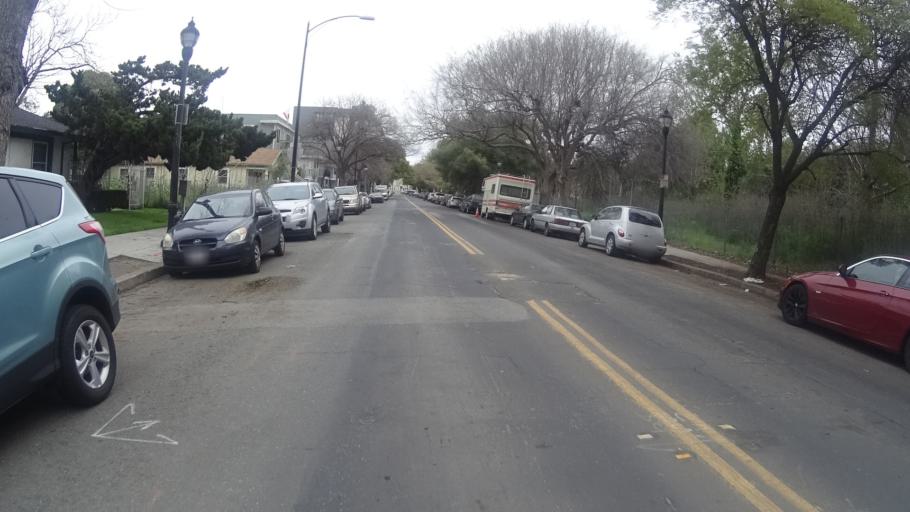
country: US
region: California
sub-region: Santa Clara County
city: San Jose
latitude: 37.3257
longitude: -121.8861
